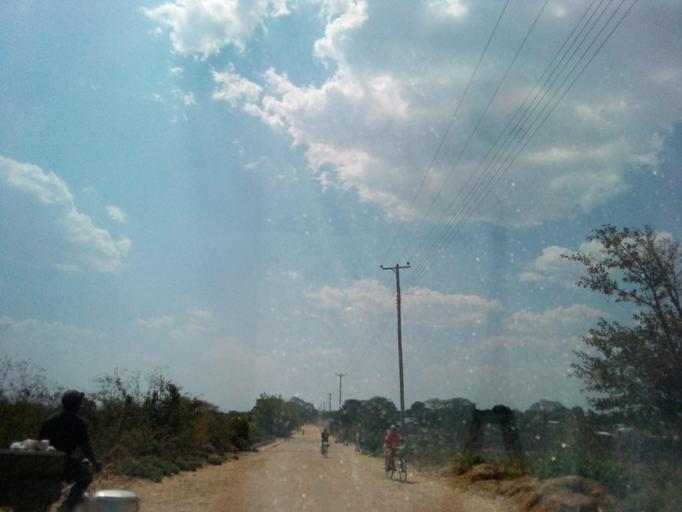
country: ZM
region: Northern
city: Mpika
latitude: -11.8458
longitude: 31.3889
